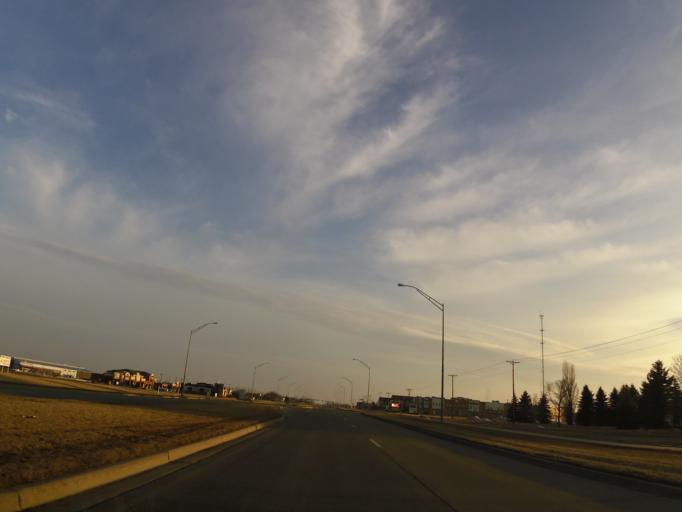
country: US
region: North Dakota
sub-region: Grand Forks County
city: Grand Forks
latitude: 47.8808
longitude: -97.0454
